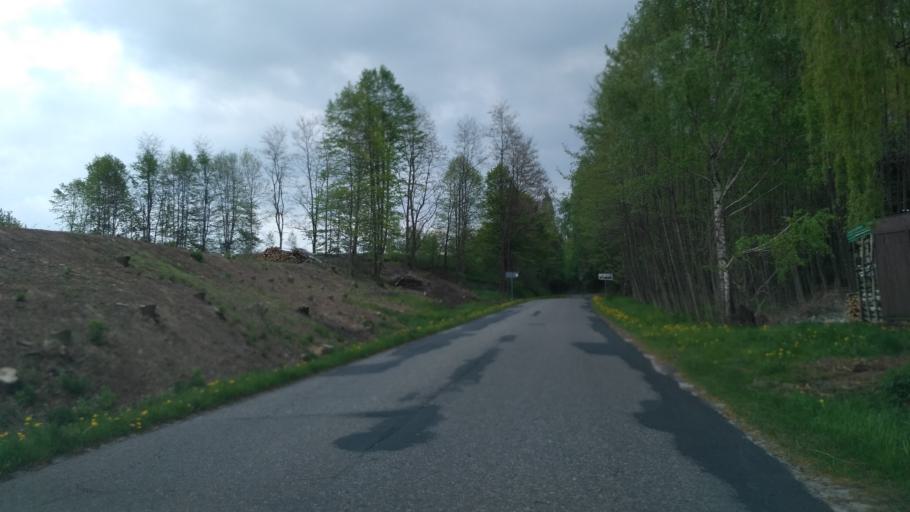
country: PL
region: Lesser Poland Voivodeship
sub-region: Powiat tarnowski
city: Szynwald
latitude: 49.9874
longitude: 21.1200
